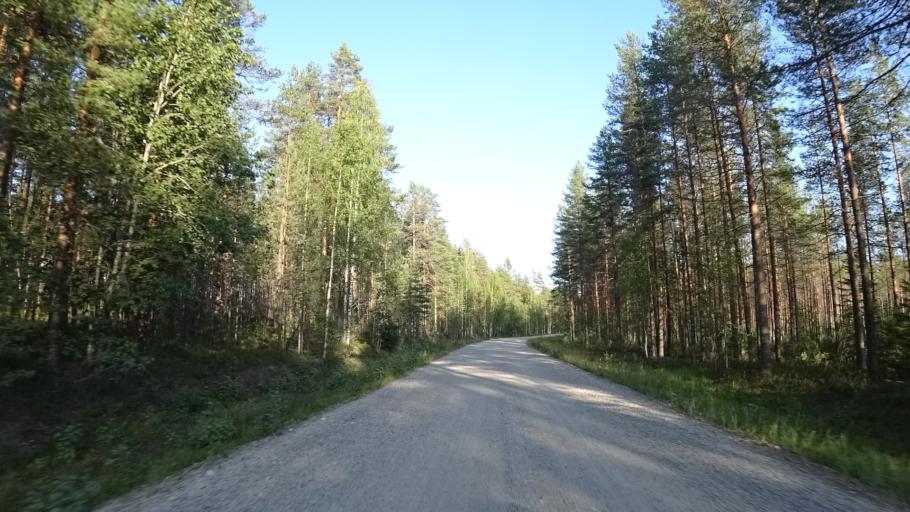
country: FI
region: North Karelia
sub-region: Joensuu
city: Ilomantsi
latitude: 63.1373
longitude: 30.7017
